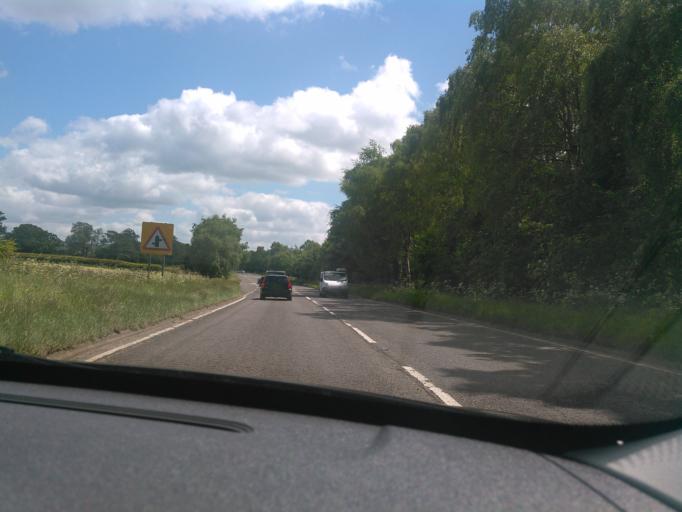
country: GB
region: England
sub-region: Shropshire
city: Market Drayton
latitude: 52.9105
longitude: -2.4716
